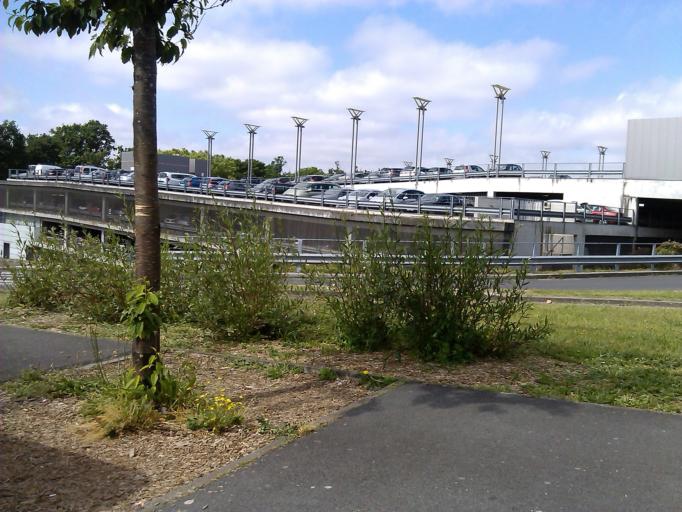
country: FR
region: Aquitaine
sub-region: Departement de la Gironde
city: Cenon
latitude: 44.8650
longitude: -0.5237
